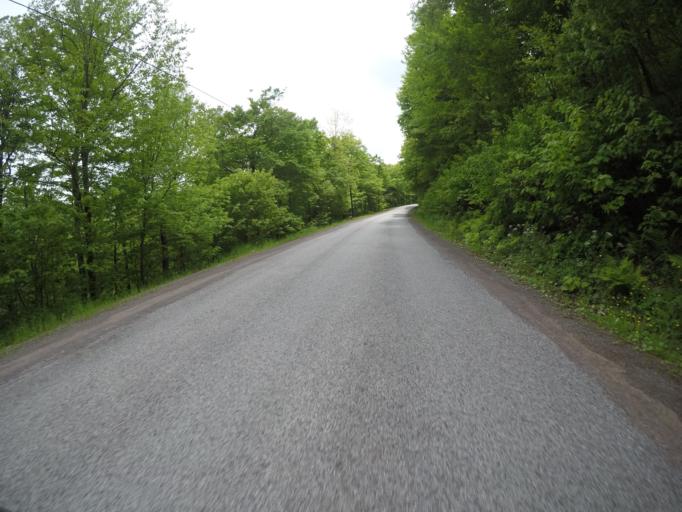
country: US
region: New York
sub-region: Delaware County
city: Stamford
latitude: 42.2551
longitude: -74.7090
